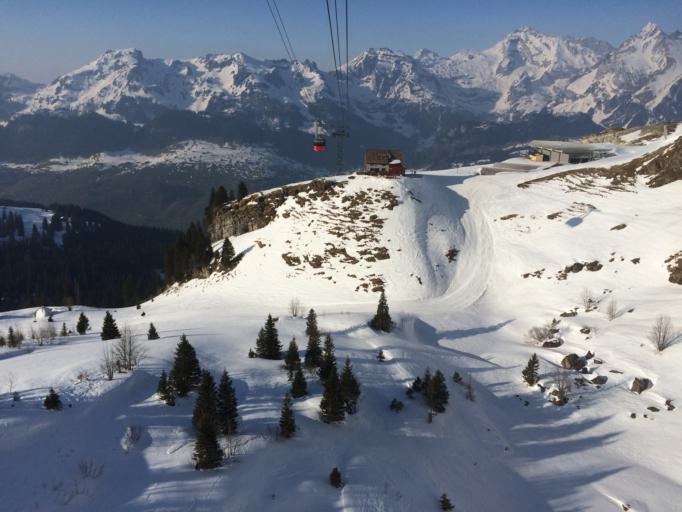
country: CH
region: Saint Gallen
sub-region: Wahlkreis Sarganserland
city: Walenstadt
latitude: 47.1694
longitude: 9.3120
